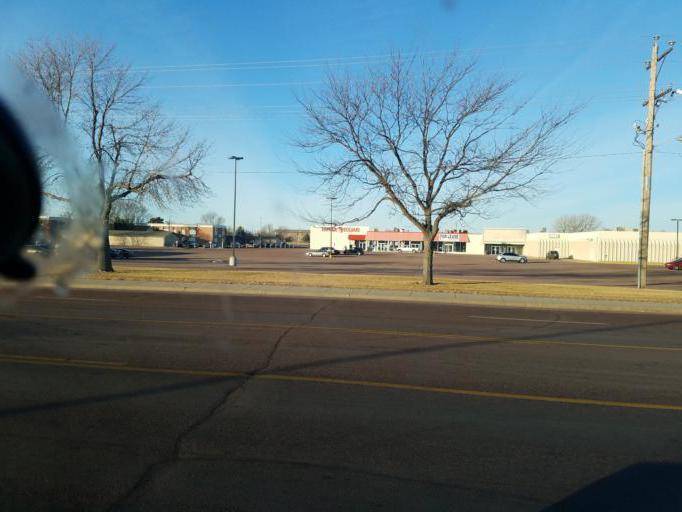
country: US
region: South Dakota
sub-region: Davison County
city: Mitchell
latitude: 43.7262
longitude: -98.0257
